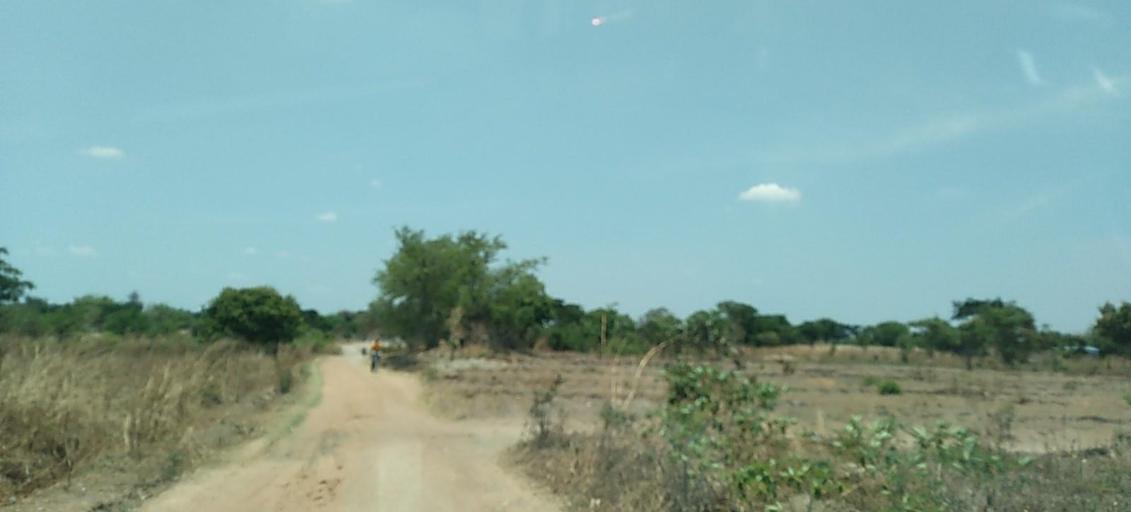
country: ZM
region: Copperbelt
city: Luanshya
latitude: -13.0730
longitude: 28.4055
